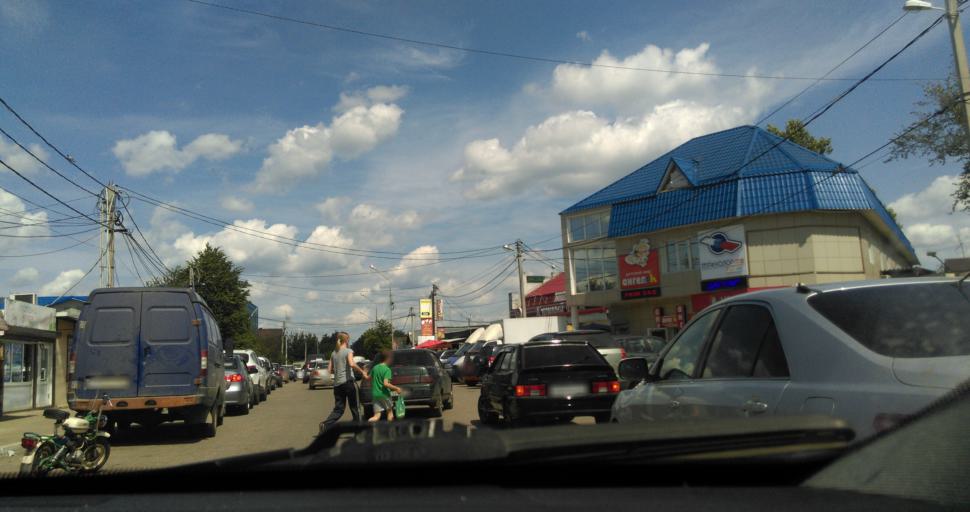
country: RU
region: Moskovskaya
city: Tuchkovo
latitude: 55.5984
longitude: 36.4695
